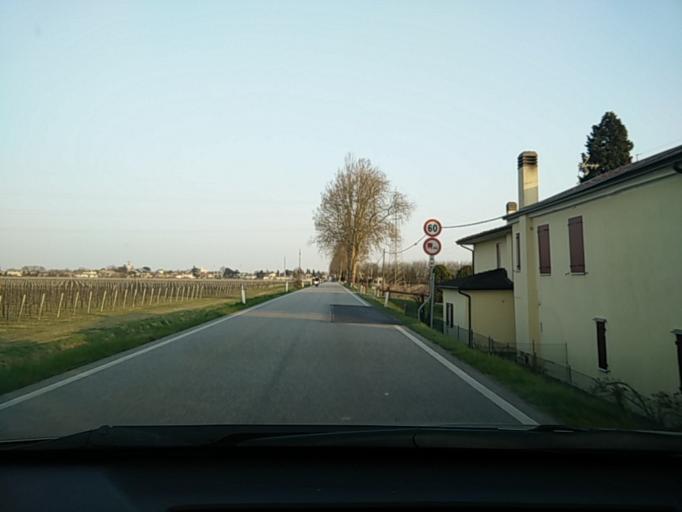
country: IT
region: Veneto
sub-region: Provincia di Treviso
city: Zenson di Piave
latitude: 45.6816
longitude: 12.4778
